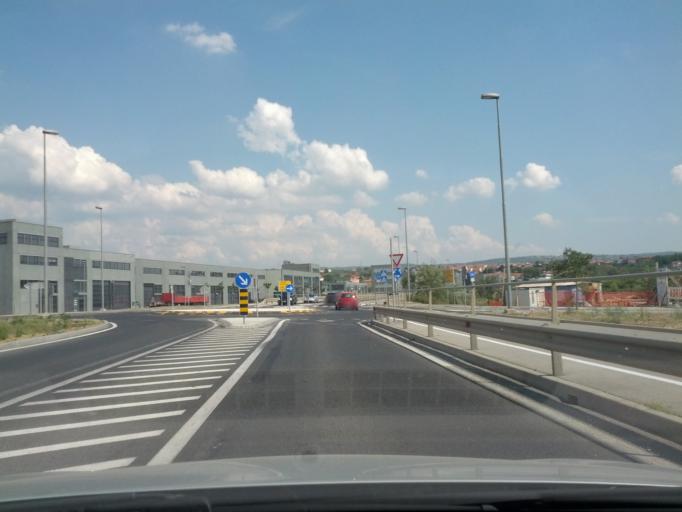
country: SI
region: Koper-Capodistria
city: Prade
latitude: 45.5514
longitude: 13.7603
